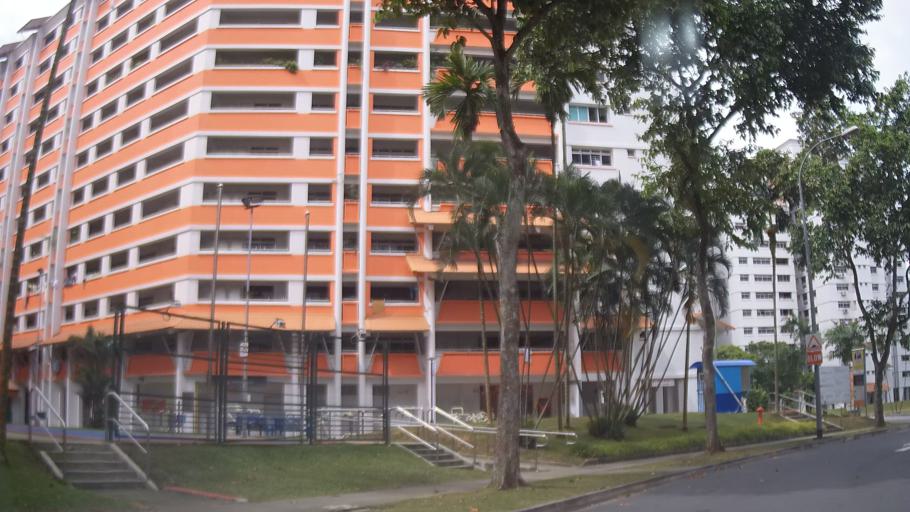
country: MY
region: Johor
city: Johor Bahru
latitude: 1.3894
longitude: 103.7425
